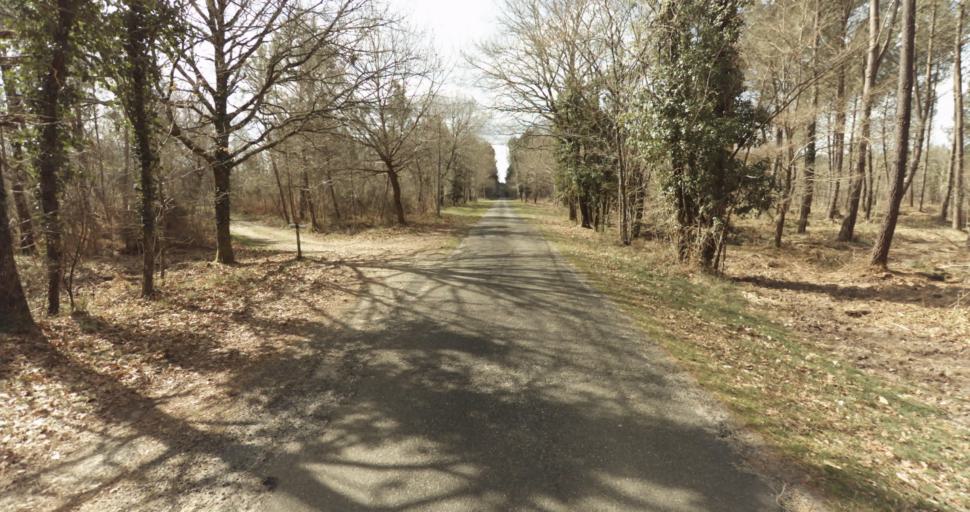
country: FR
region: Aquitaine
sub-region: Departement des Landes
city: Roquefort
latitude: 44.0424
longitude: -0.3734
